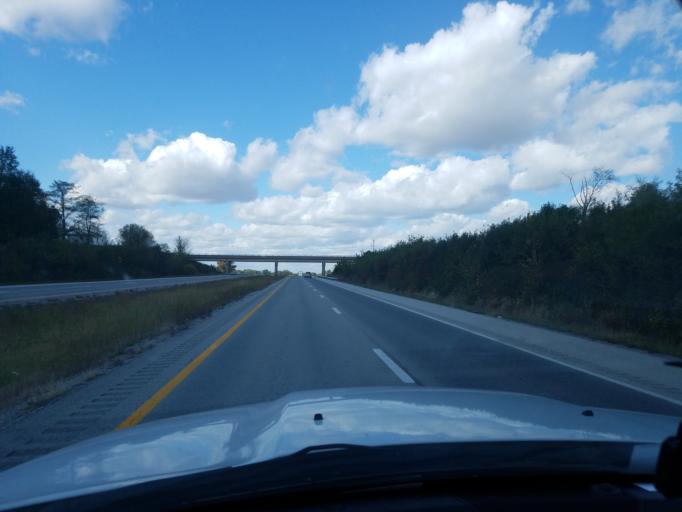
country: US
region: Kentucky
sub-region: Daviess County
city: Masonville
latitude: 37.6609
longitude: -87.0127
